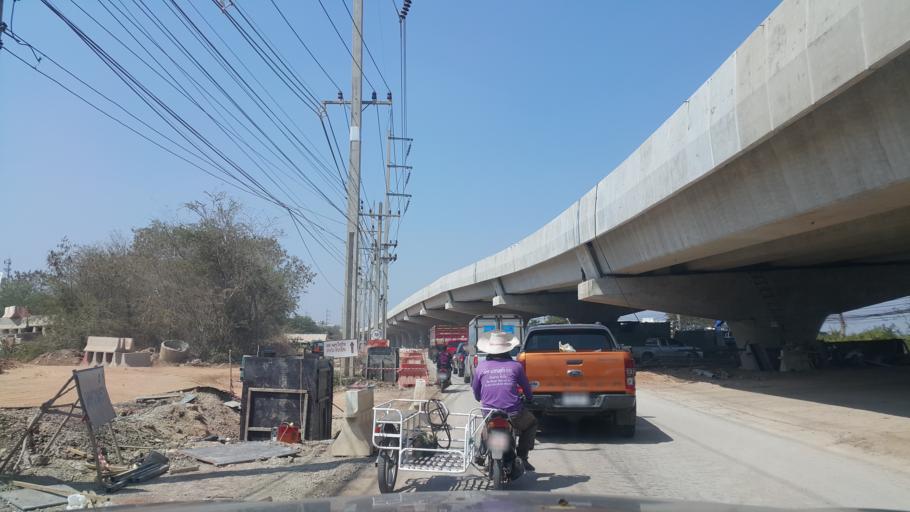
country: TH
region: Nakhon Ratchasima
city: Bua Yai
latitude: 15.5901
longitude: 102.4336
